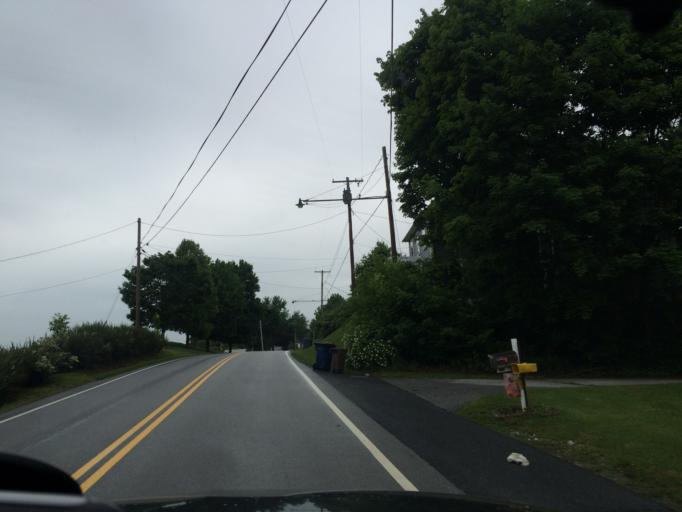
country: US
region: Maryland
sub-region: Carroll County
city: New Windsor
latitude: 39.5939
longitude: -77.1064
